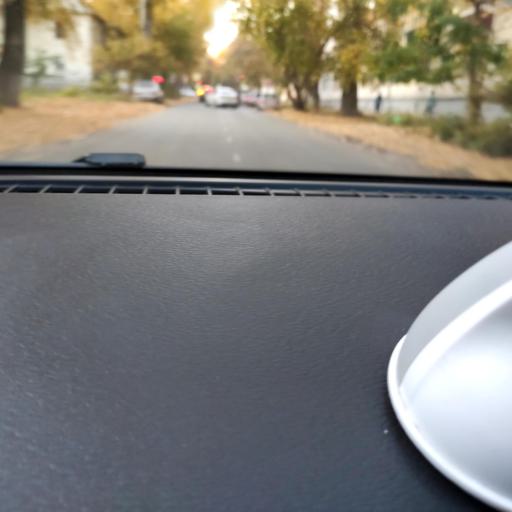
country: RU
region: Samara
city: Samara
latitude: 53.2251
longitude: 50.2621
